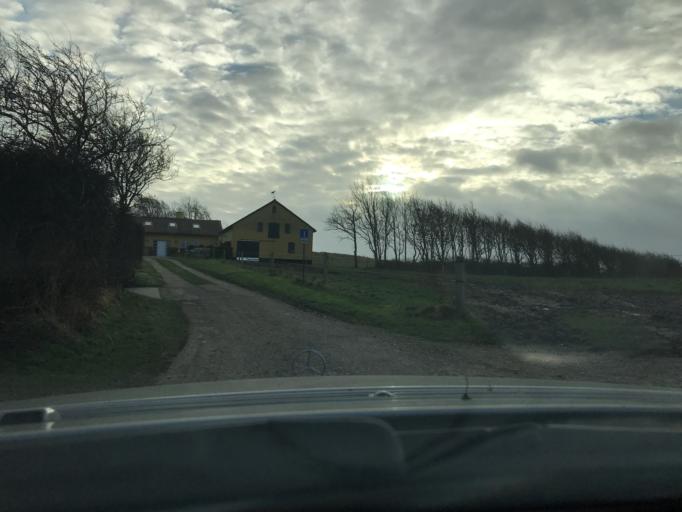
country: DK
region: South Denmark
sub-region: Sonderborg Kommune
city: Nordborg
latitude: 55.0518
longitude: 9.6409
